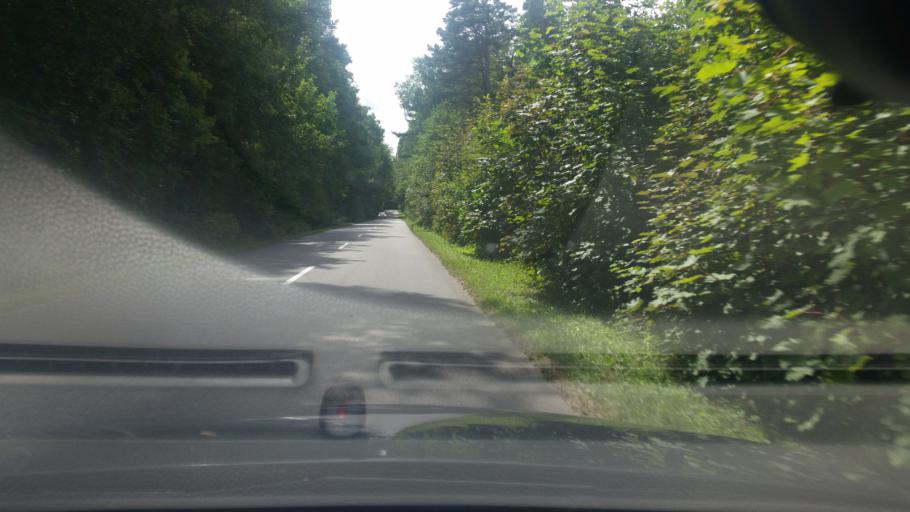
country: PL
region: Pomeranian Voivodeship
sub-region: Powiat wejherowski
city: Choczewo
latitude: 54.7515
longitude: 17.7467
